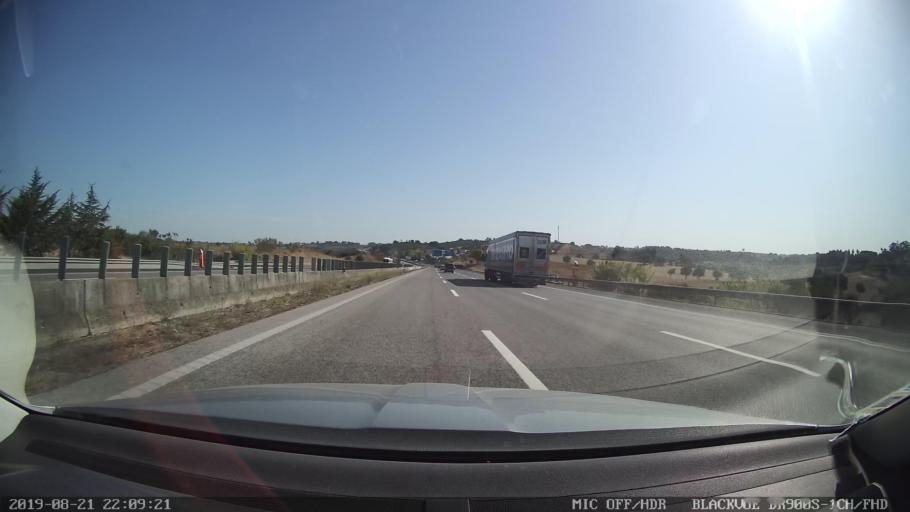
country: PT
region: Lisbon
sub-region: Azambuja
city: Aveiras de Cima
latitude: 39.1283
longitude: -8.9020
